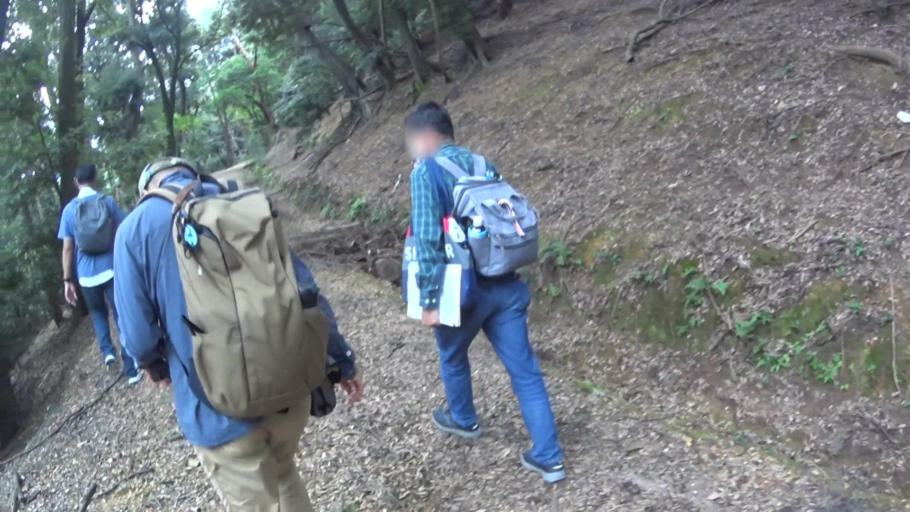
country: JP
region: Osaka
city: Kishiwada
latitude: 34.5016
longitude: 135.3342
